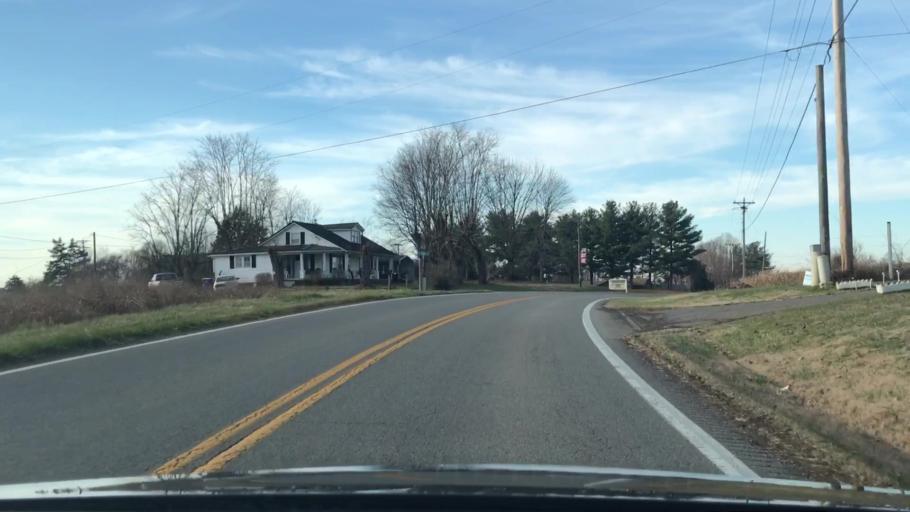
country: US
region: Kentucky
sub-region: Monroe County
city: Tompkinsville
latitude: 36.6367
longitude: -85.7750
